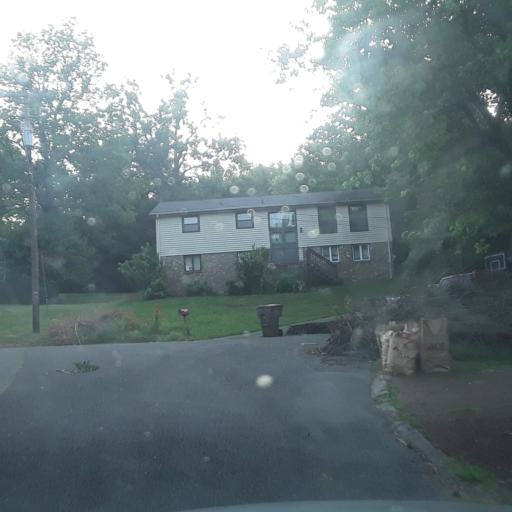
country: US
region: Tennessee
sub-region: Williamson County
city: Brentwood Estates
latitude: 36.0503
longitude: -86.7306
